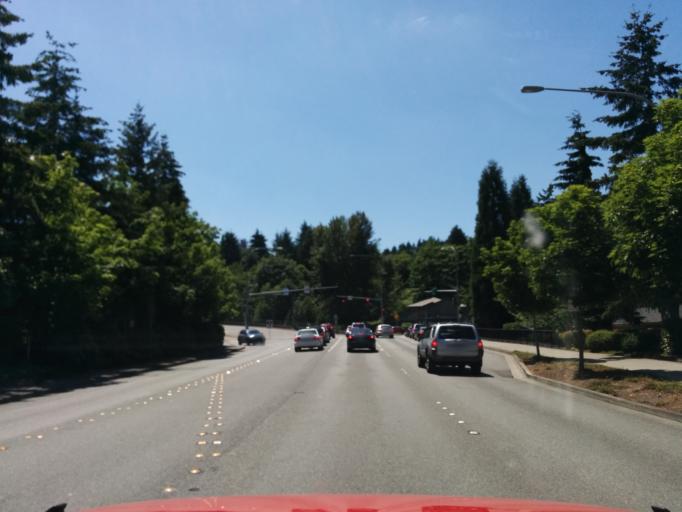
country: US
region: Washington
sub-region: King County
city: Redmond
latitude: 47.6700
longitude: -122.1286
